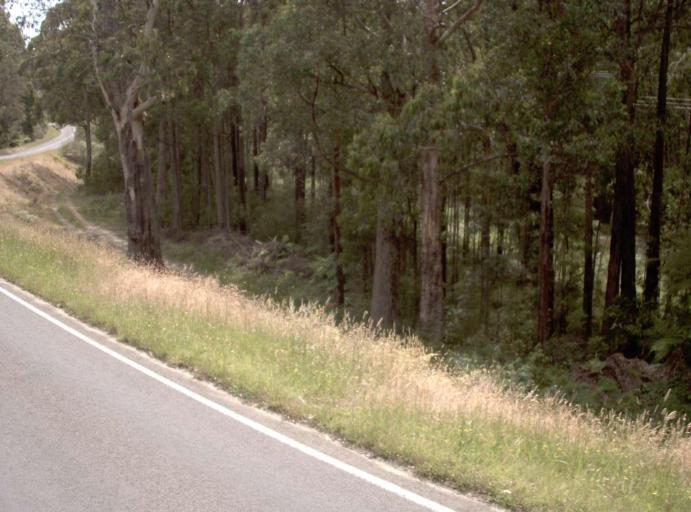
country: AU
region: Victoria
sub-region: Latrobe
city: Moe
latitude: -37.9416
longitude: 146.3995
